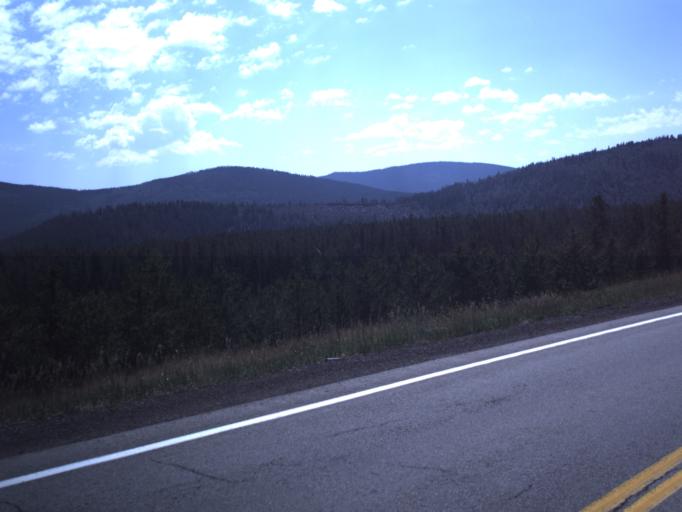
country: US
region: Utah
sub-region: Daggett County
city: Manila
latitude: 40.8340
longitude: -109.4626
